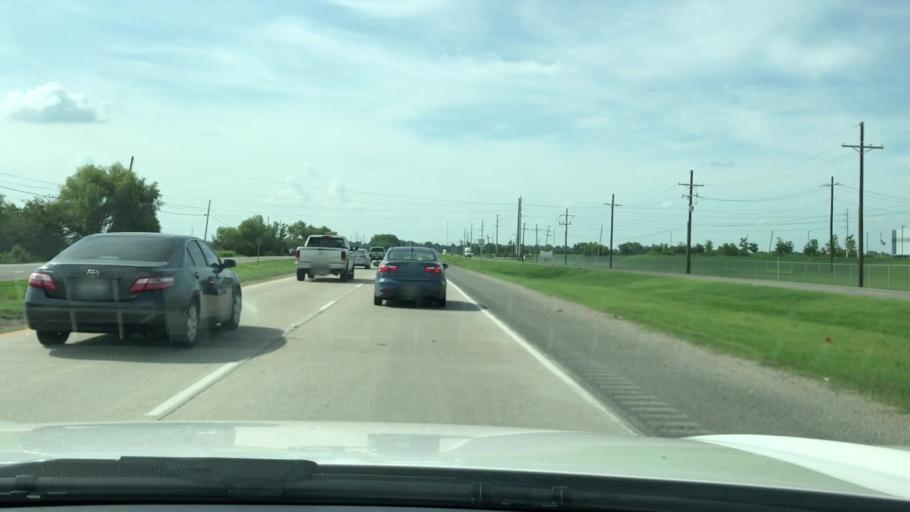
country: US
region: Louisiana
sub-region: West Baton Rouge Parish
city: Addis
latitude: 30.3345
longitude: -91.2578
